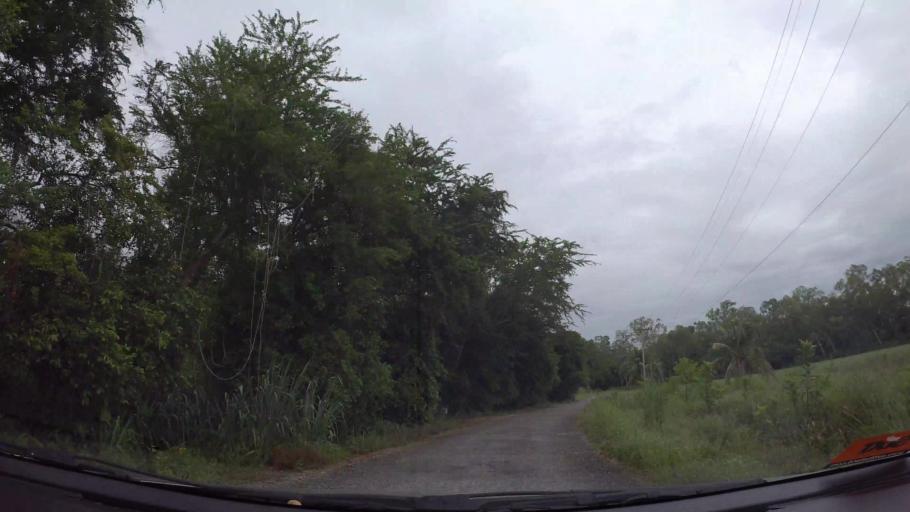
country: TH
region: Chon Buri
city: Si Racha
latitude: 13.1968
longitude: 100.9951
